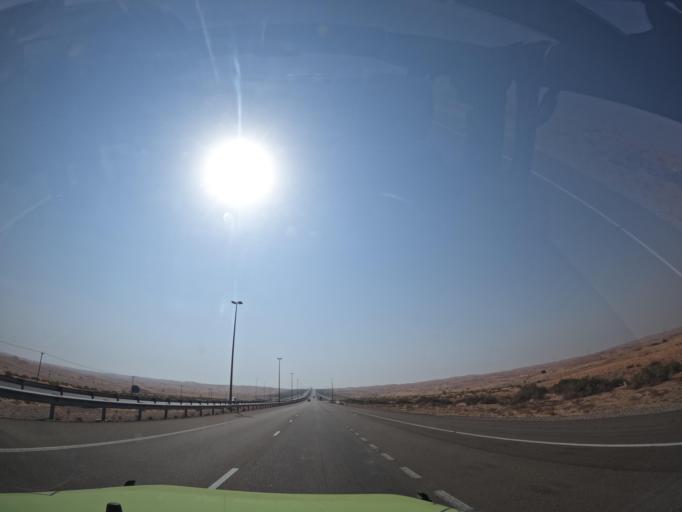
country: OM
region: Al Buraimi
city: Al Buraymi
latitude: 24.4417
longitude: 55.6635
